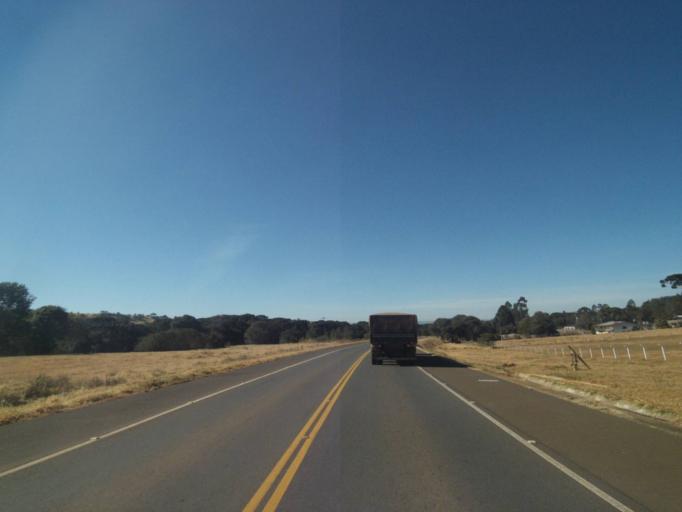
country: BR
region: Parana
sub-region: Tibagi
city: Tibagi
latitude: -24.5805
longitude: -50.4425
